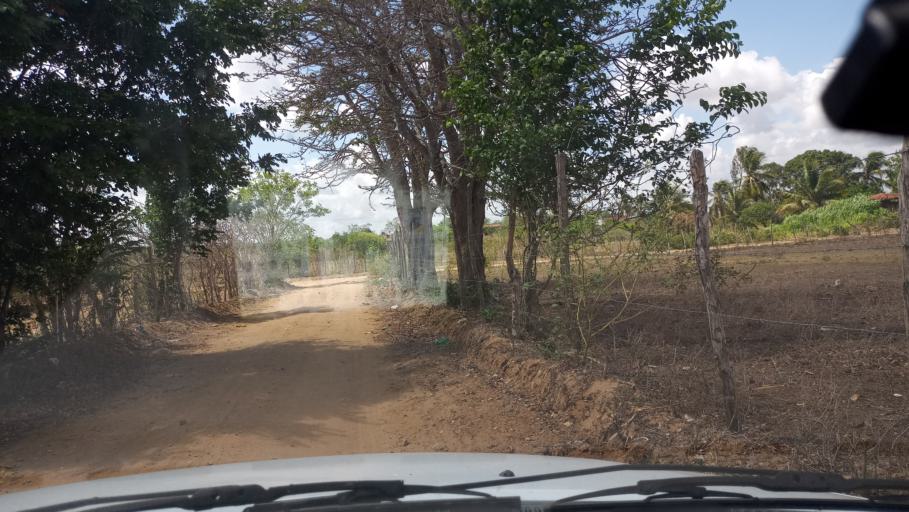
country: BR
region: Rio Grande do Norte
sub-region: Santo Antonio
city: Santo Antonio
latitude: -6.3477
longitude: -35.3702
